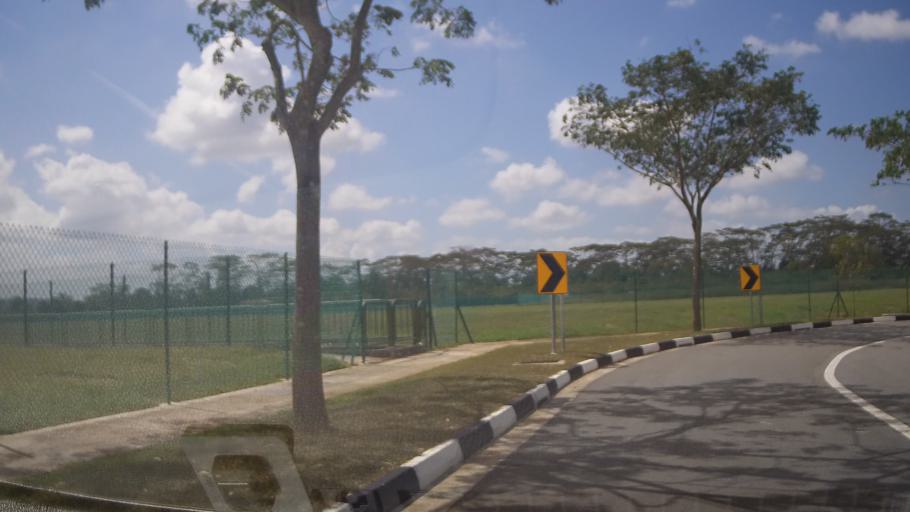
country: MY
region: Johor
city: Johor Bahru
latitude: 1.4205
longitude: 103.7252
